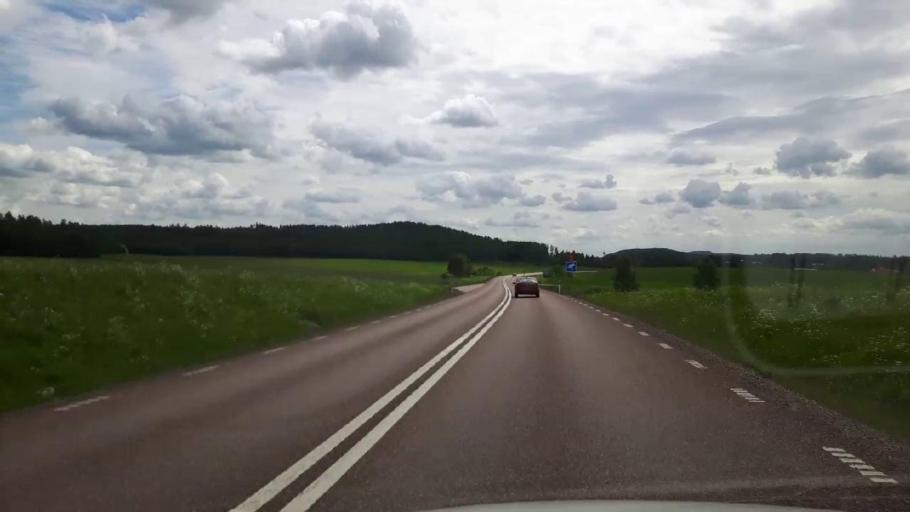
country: SE
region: Dalarna
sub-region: Hedemora Kommun
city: Hedemora
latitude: 60.3334
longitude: 15.9461
